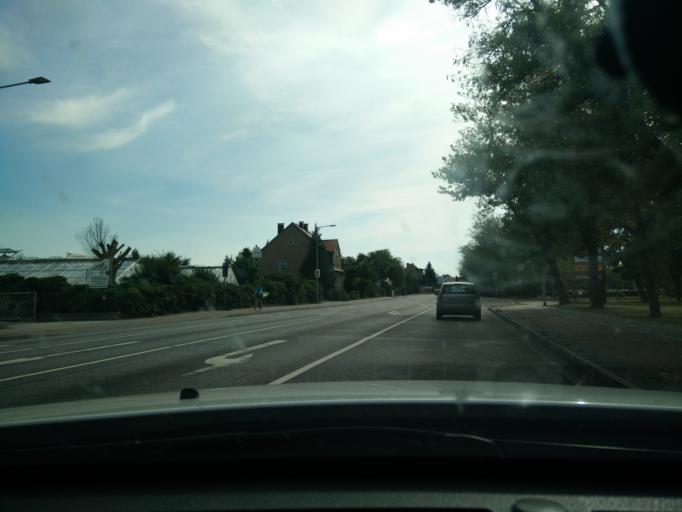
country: DE
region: Saxony-Anhalt
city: Burg bei Magdeburg
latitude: 52.2645
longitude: 11.8464
